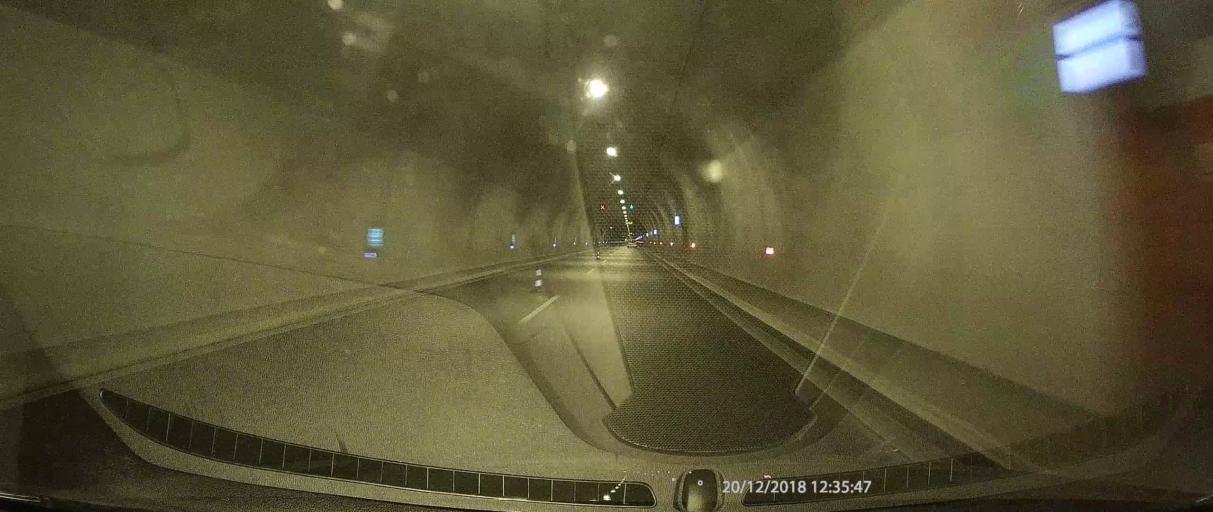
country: GR
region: West Greece
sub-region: Nomos Aitolias kai Akarnanias
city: Antirrio
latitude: 38.3546
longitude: 21.6896
